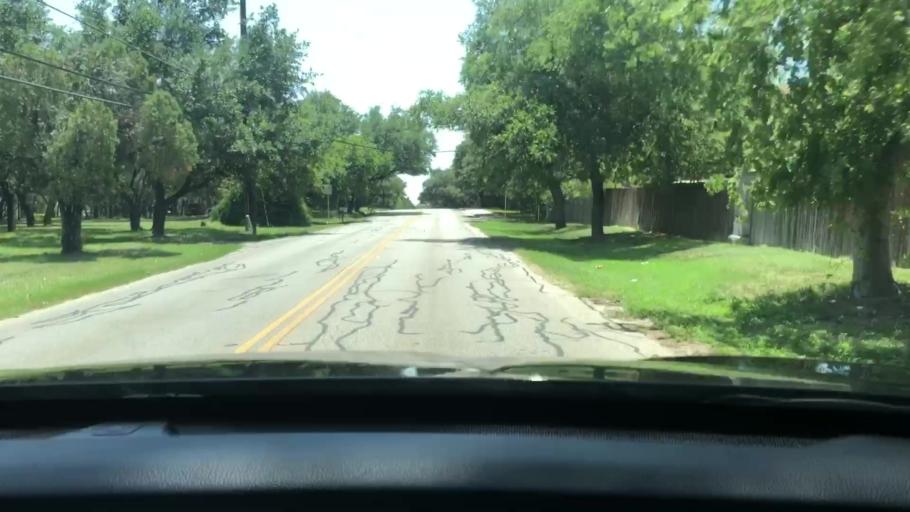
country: US
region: Texas
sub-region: Bexar County
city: Helotes
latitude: 29.5472
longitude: -98.6558
